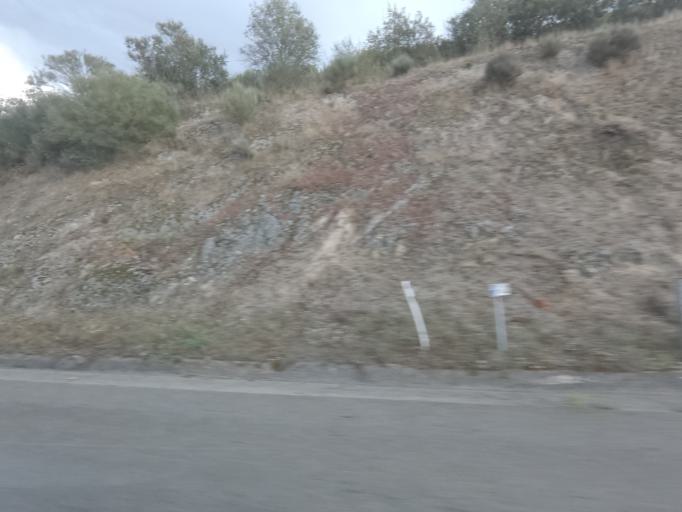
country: PT
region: Viseu
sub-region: Tarouca
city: Tarouca
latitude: 41.0171
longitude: -7.8819
